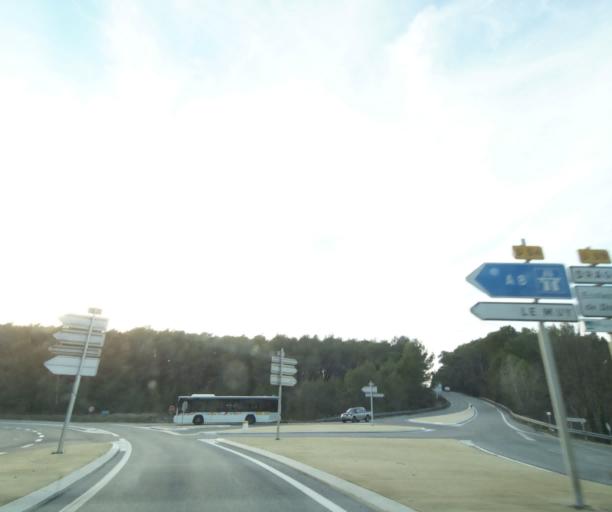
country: FR
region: Provence-Alpes-Cote d'Azur
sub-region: Departement du Var
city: La Motte
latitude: 43.5242
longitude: 6.5261
